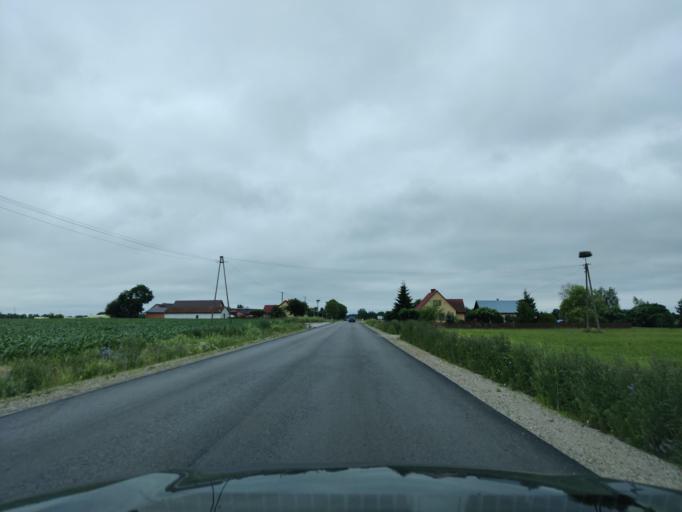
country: PL
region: Warmian-Masurian Voivodeship
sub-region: Powiat szczycienski
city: Rozogi
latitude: 53.4605
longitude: 21.3695
